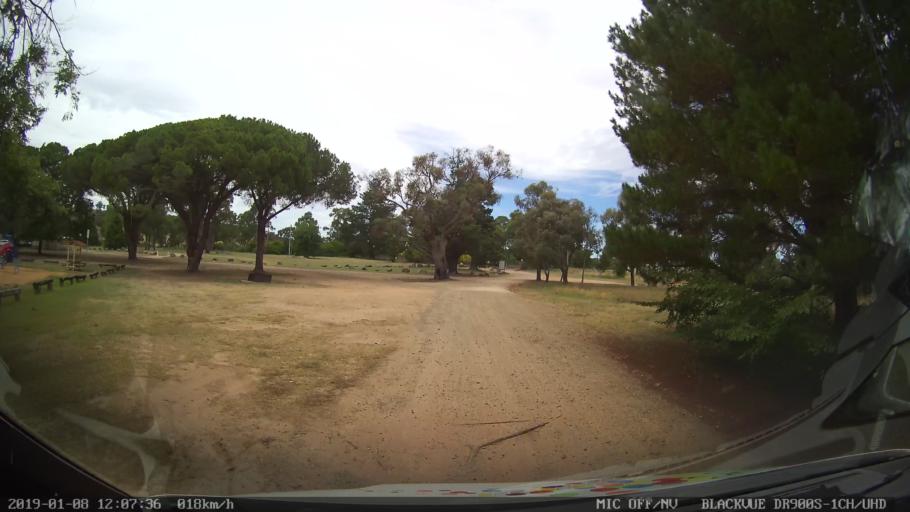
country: AU
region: New South Wales
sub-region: Armidale Dumaresq
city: Armidale
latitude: -30.4287
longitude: 151.5941
